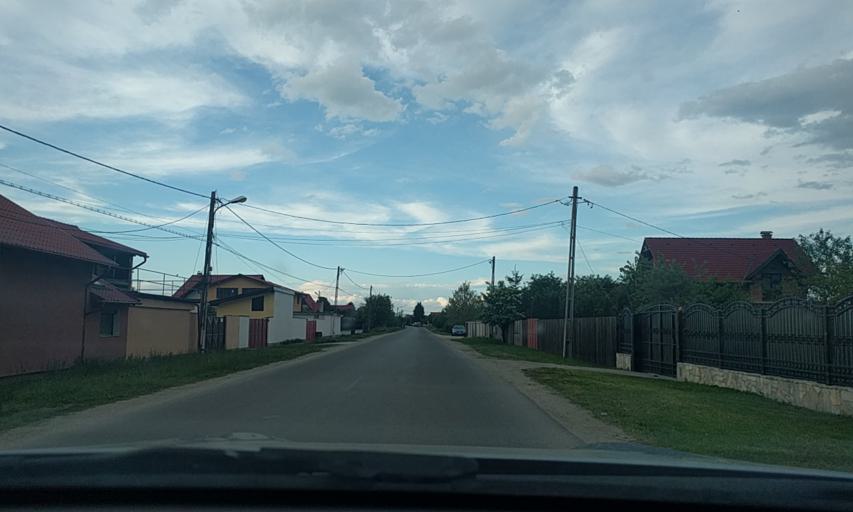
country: RO
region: Brasov
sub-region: Comuna Harman
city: Harman
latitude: 45.7580
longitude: 25.7197
